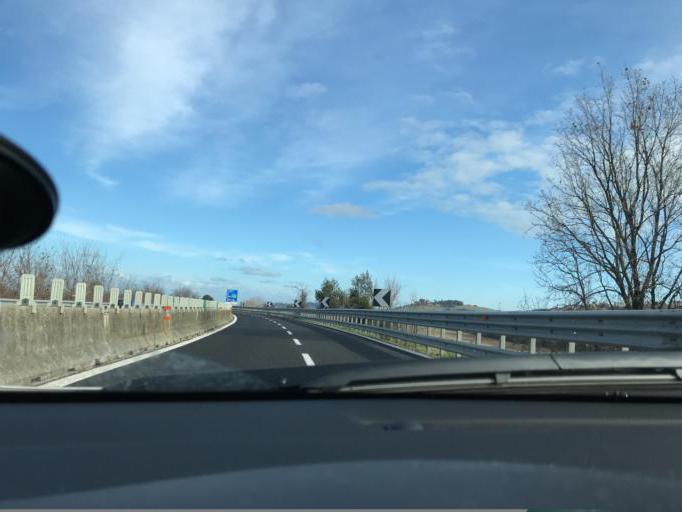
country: IT
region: The Marches
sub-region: Provincia di Ancona
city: Camerata Picena
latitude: 43.5897
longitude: 13.3497
